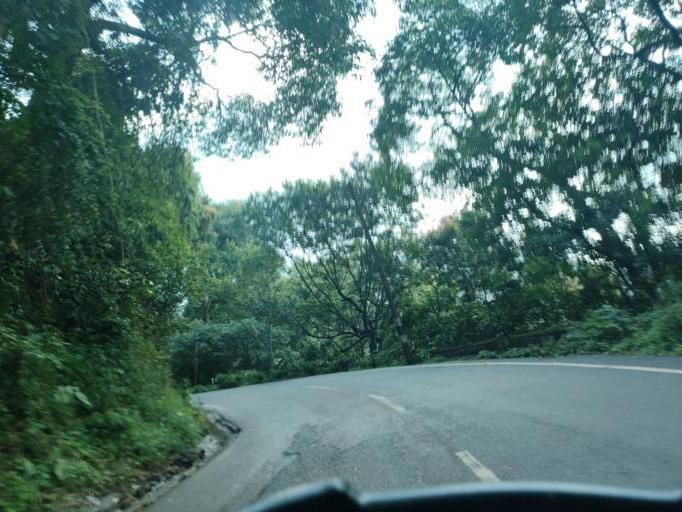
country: IN
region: Tamil Nadu
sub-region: Dindigul
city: Kodaikanal
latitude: 10.2563
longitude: 77.5308
